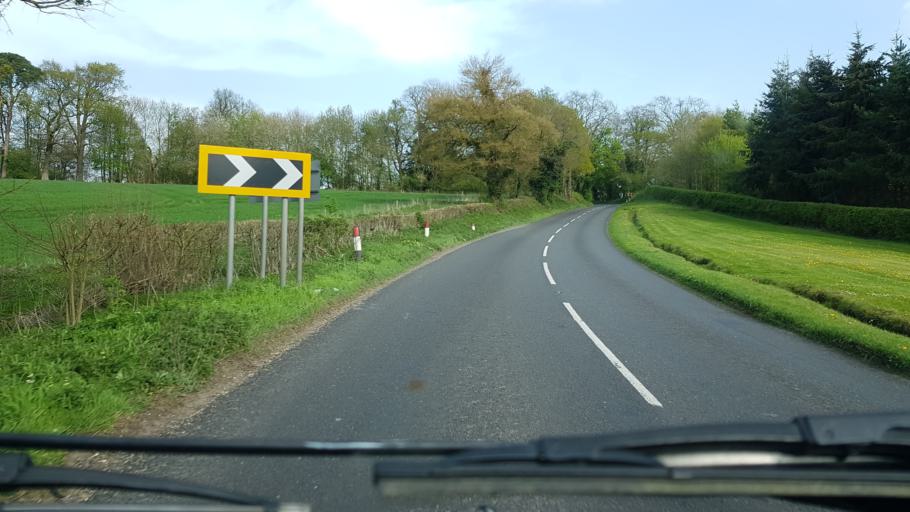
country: GB
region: England
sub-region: Hampshire
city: Overton
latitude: 51.2451
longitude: -1.2249
